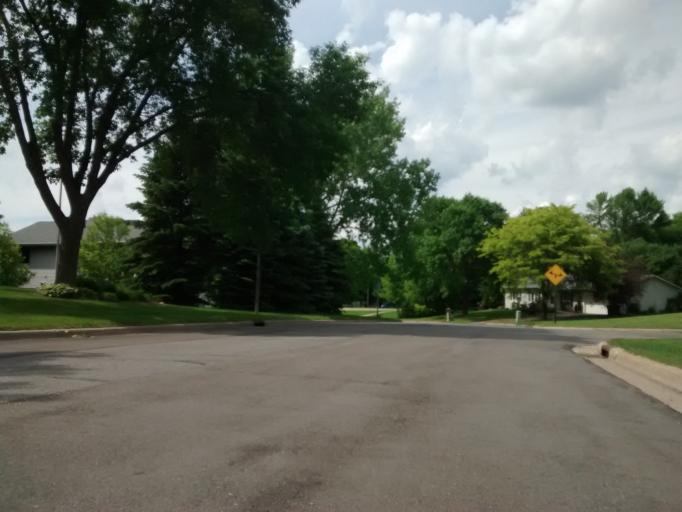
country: US
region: Minnesota
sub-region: Dakota County
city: Burnsville
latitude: 44.7526
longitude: -93.2948
